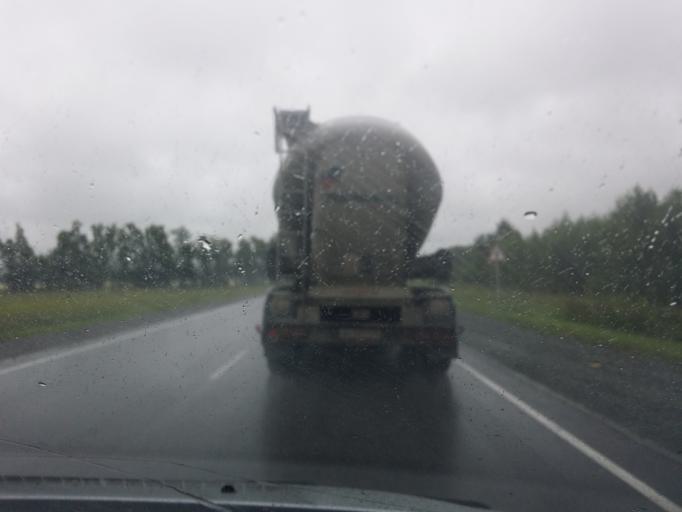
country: RU
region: Altai Krai
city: Bayunovskiye Klyuchi
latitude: 53.3015
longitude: 84.2686
